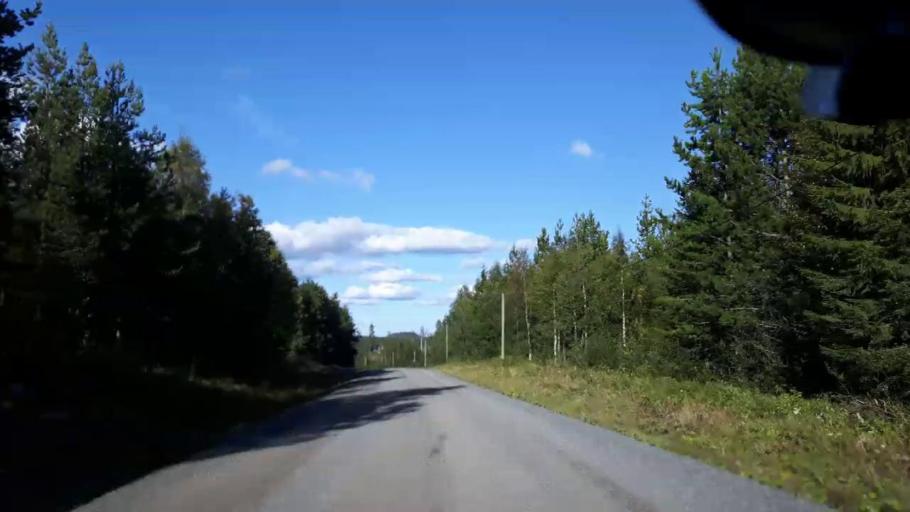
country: SE
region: Jaemtland
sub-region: Ragunda Kommun
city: Hammarstrand
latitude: 63.4485
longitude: 16.2243
